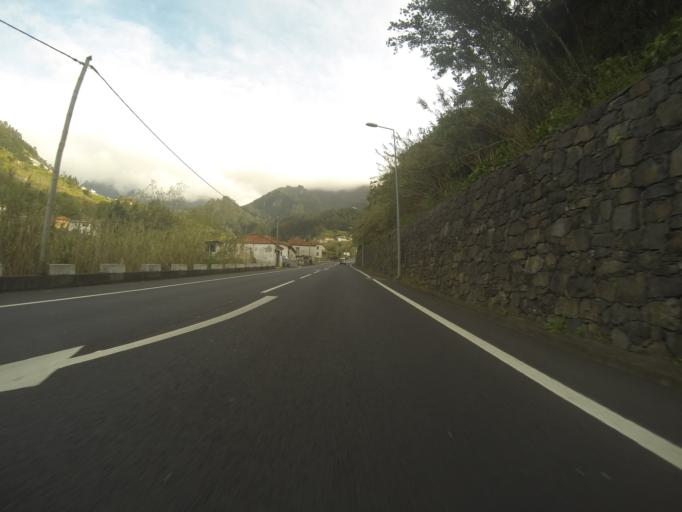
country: PT
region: Madeira
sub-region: Sao Vicente
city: Sao Vicente
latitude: 32.7772
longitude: -17.0330
